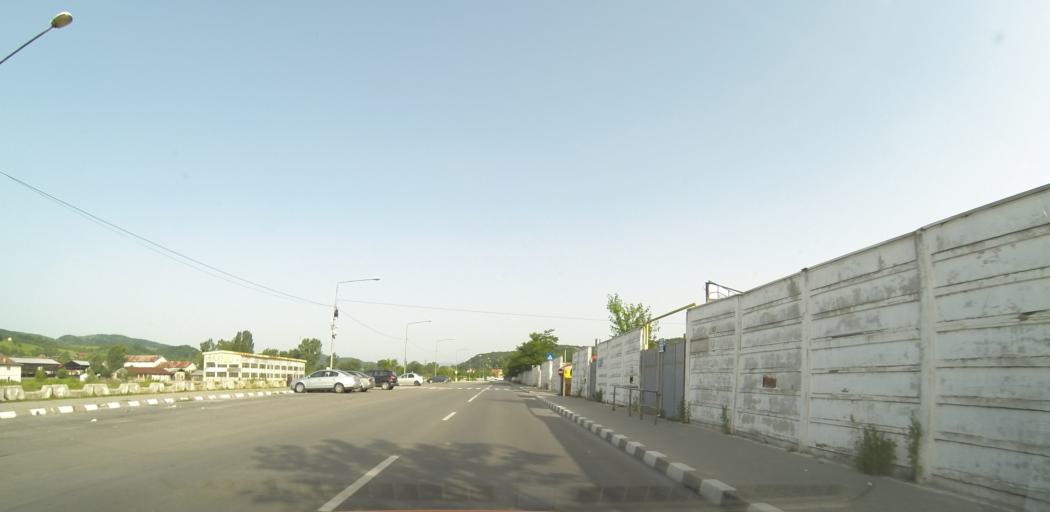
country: RO
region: Valcea
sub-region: Municipiul Ramnicu Valcea
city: Ramnicu Valcea
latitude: 45.1025
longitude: 24.3515
